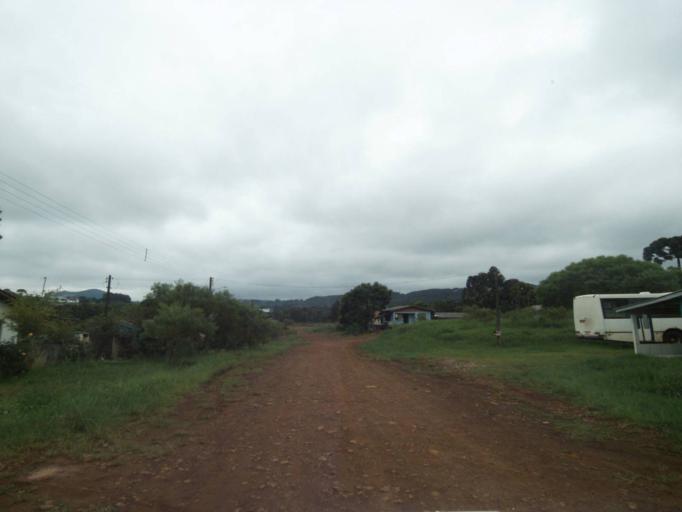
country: BR
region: Parana
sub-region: Pitanga
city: Pitanga
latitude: -24.9379
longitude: -51.8734
